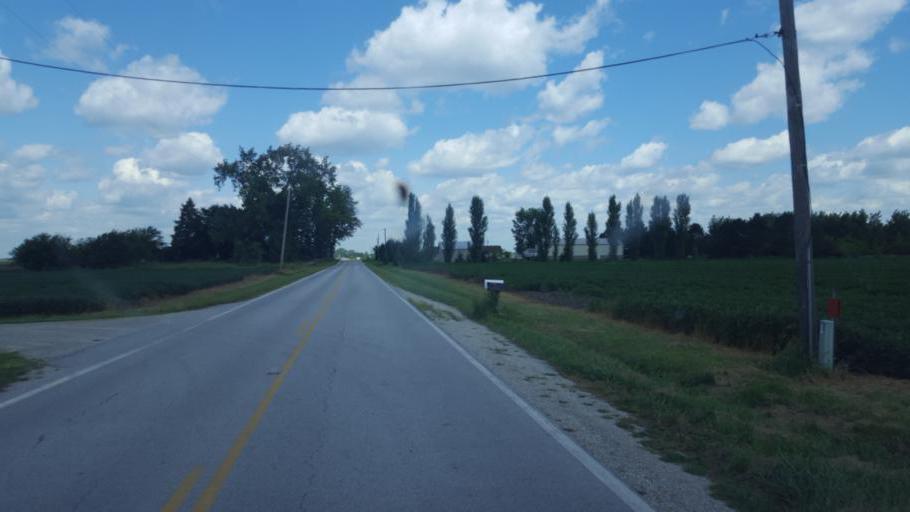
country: US
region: Ohio
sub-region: Sandusky County
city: Gibsonburg
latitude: 41.2753
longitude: -83.3116
